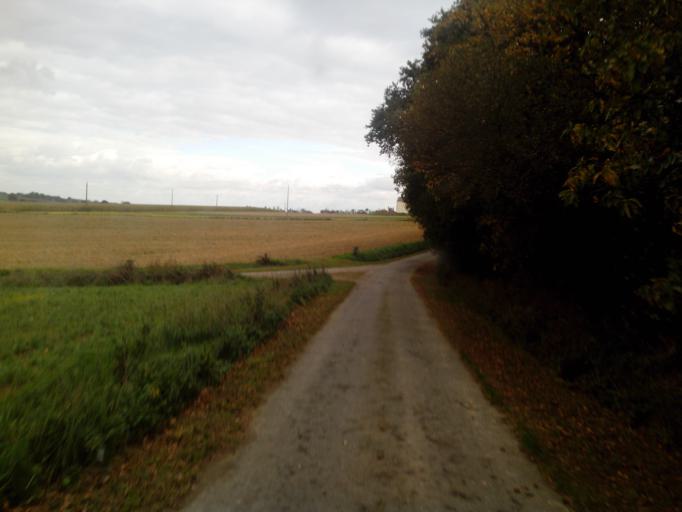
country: FR
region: Brittany
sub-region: Departement du Morbihan
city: Mauron
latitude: 48.0641
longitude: -2.3182
